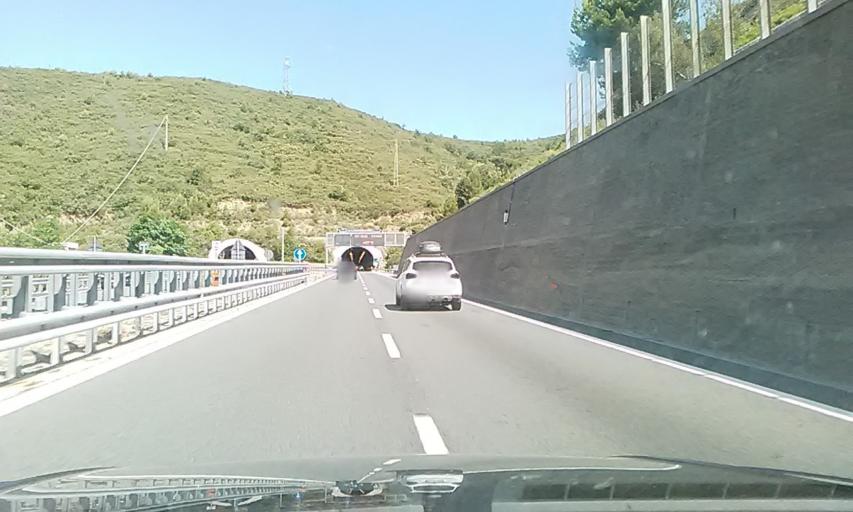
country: IT
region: Liguria
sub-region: Provincia di Savona
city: Laigueglia
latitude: 43.9962
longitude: 8.1353
